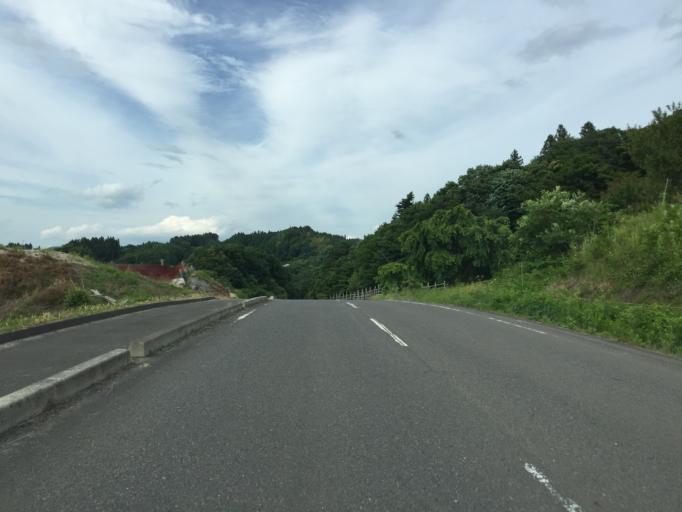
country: JP
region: Fukushima
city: Funehikimachi-funehiki
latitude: 37.5021
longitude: 140.5559
